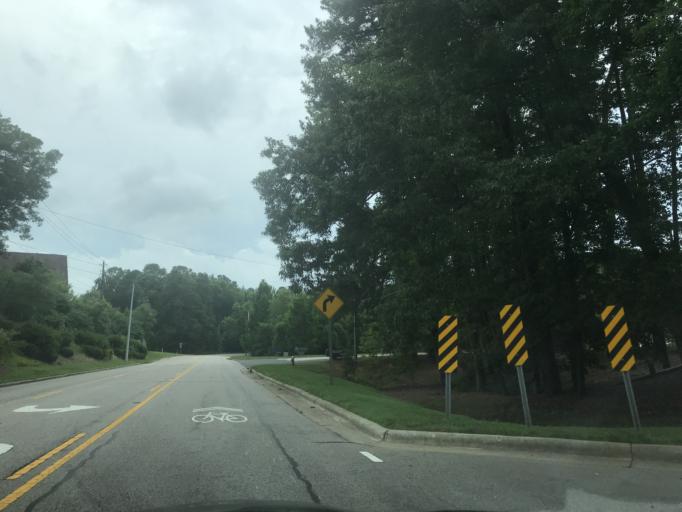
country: US
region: North Carolina
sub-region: Wake County
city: Cary
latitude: 35.7732
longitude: -78.8028
